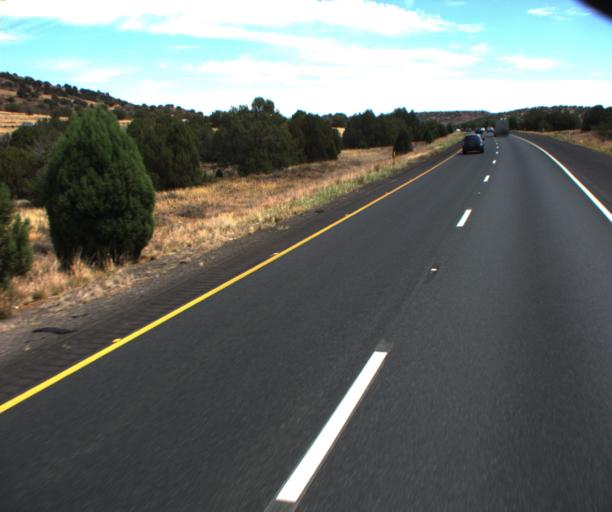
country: US
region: Arizona
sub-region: Yavapai County
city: Camp Verde
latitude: 34.4867
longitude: -112.0108
